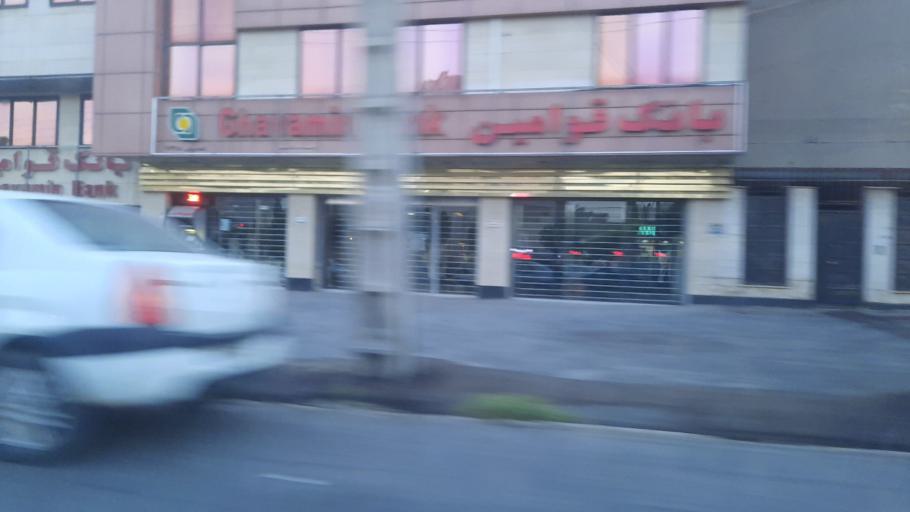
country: IR
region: Markazi
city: Arak
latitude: 34.0774
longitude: 49.6966
